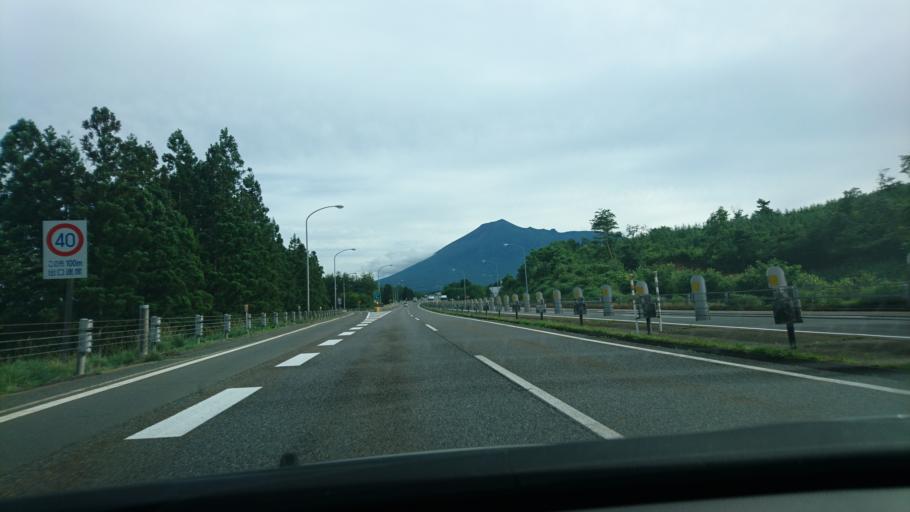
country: JP
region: Iwate
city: Shizukuishi
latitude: 39.9525
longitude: 141.0322
